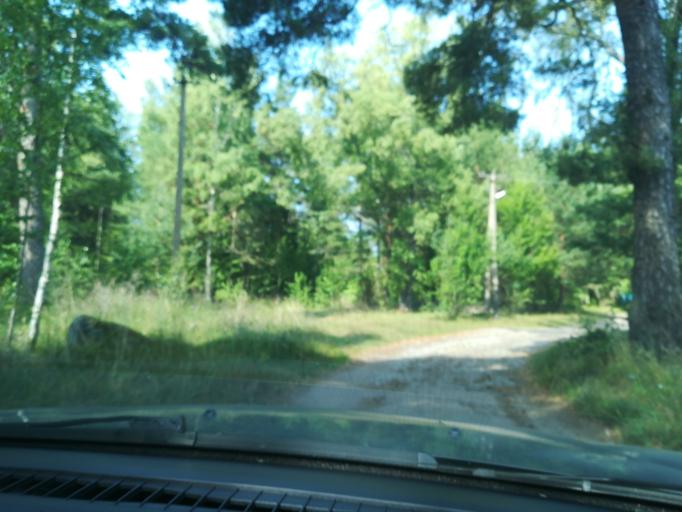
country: RU
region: Leningrad
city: Ust'-Luga
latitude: 59.7656
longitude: 28.1771
